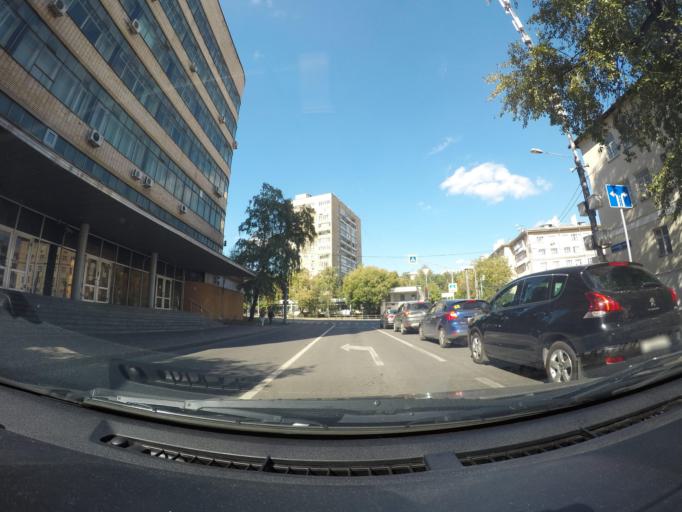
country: RU
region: Moskovskaya
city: Bogorodskoye
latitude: 55.7941
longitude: 37.6994
